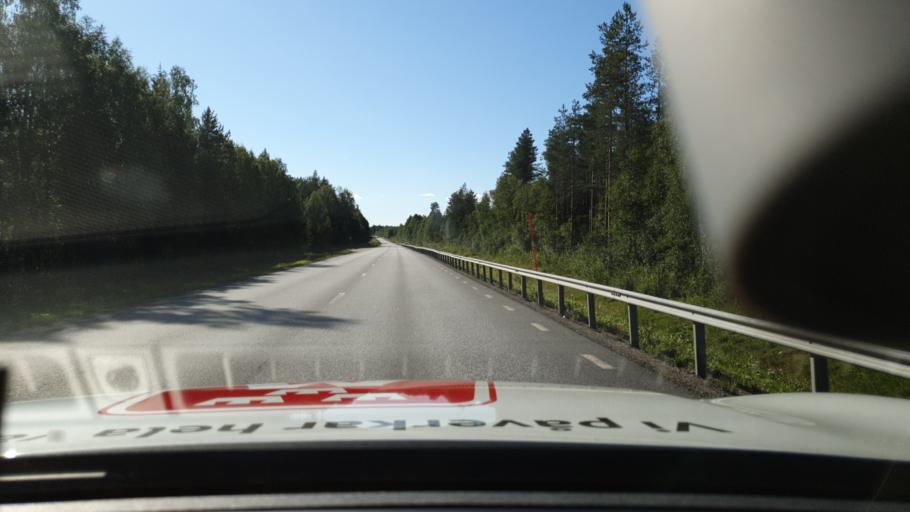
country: SE
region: Norrbotten
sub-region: Pitea Kommun
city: Rosvik
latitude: 65.5986
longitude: 21.5780
